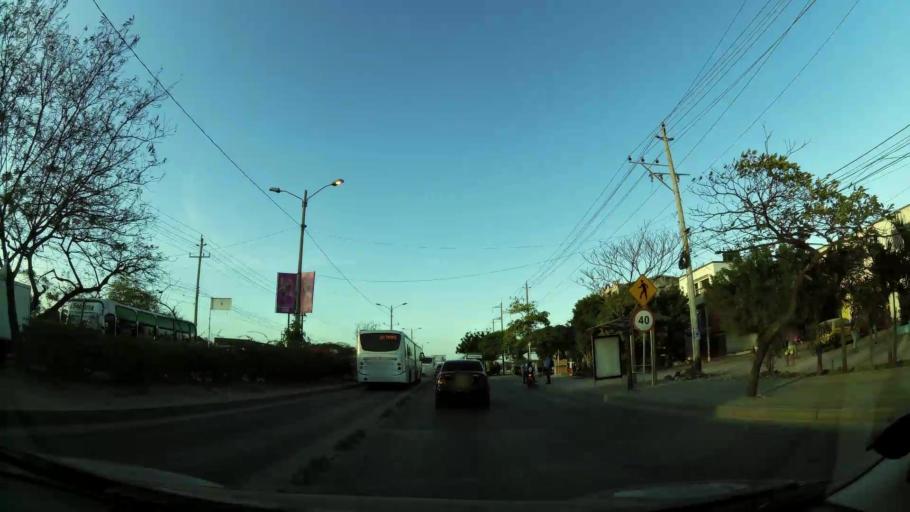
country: CO
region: Atlantico
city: Soledad
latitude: 10.9128
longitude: -74.7991
